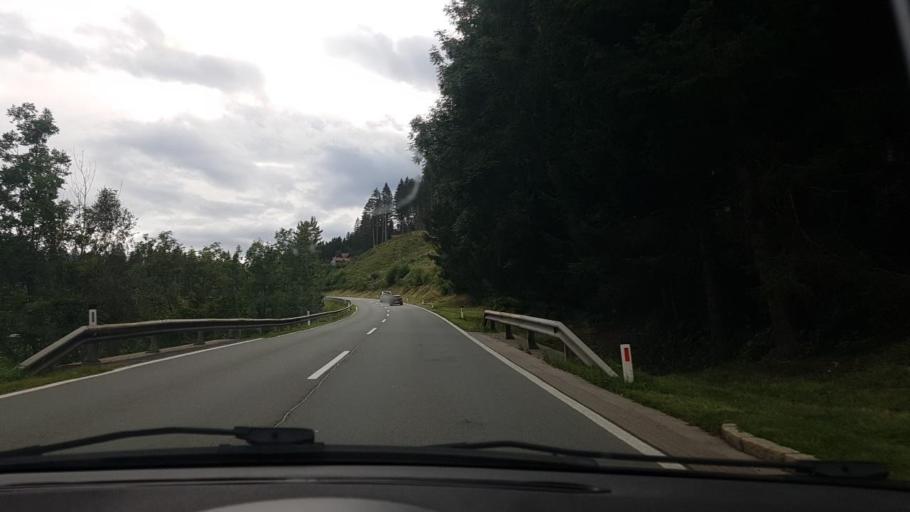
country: AT
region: Carinthia
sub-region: Politischer Bezirk Spittal an der Drau
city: Winklern
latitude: 46.8615
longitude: 12.8638
